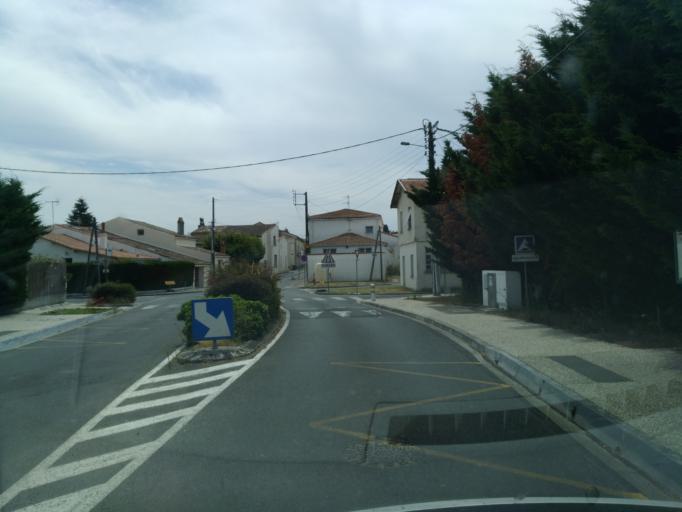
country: FR
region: Poitou-Charentes
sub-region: Departement de la Charente-Maritime
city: Saint-Palais-sur-Mer
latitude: 45.6576
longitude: -1.0767
